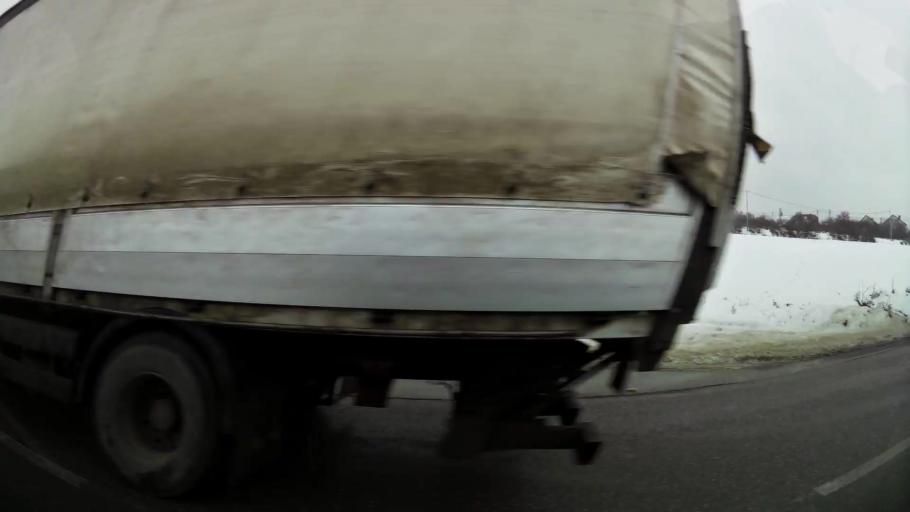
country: XK
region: Pristina
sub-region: Komuna e Prishtines
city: Pristina
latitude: 42.7254
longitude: 21.1448
